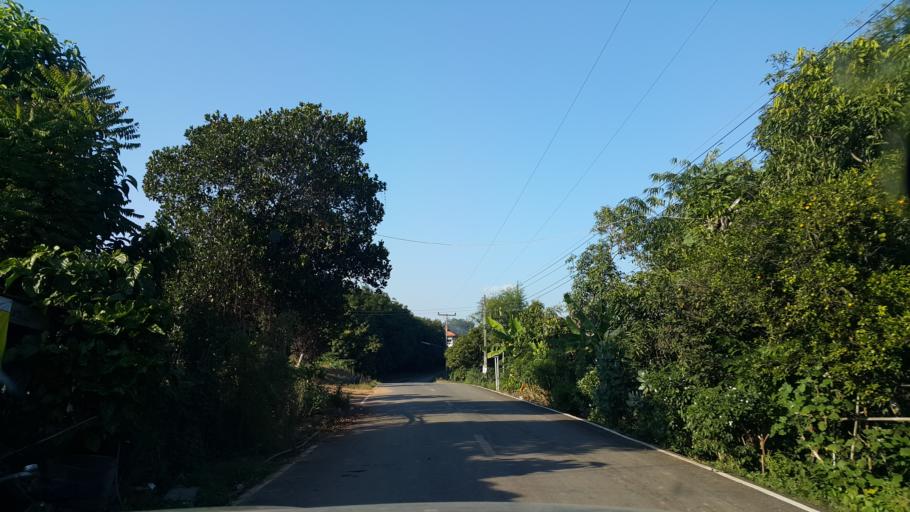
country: TH
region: Sukhothai
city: Thung Saliam
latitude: 17.4072
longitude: 99.5145
